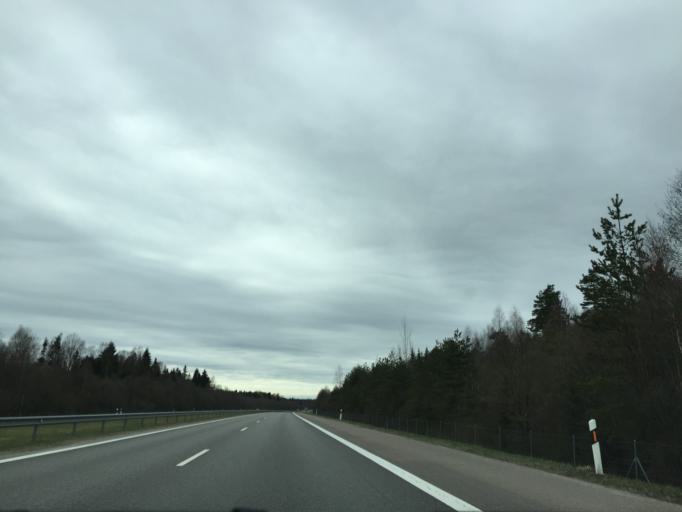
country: LT
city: Rietavas
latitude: 55.6461
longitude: 21.8320
